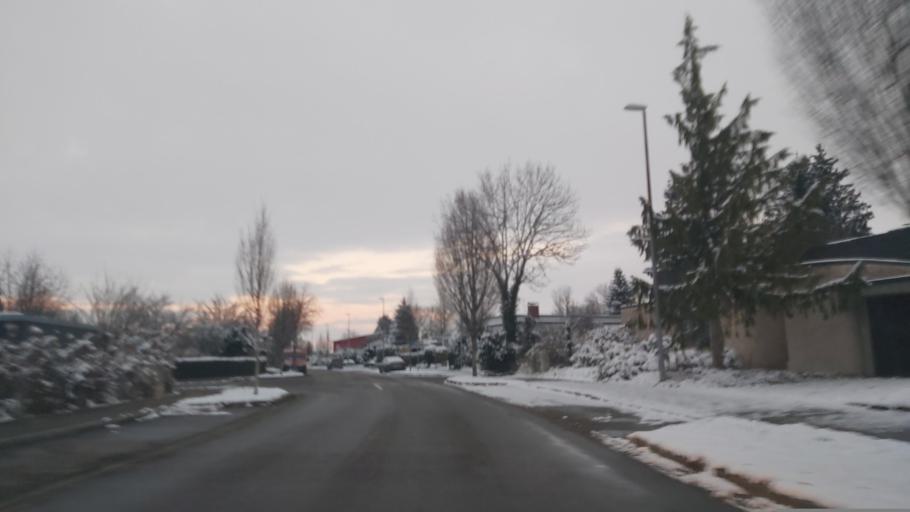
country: DE
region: Baden-Wuerttemberg
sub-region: Tuebingen Region
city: Laupheim
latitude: 48.2350
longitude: 9.8905
